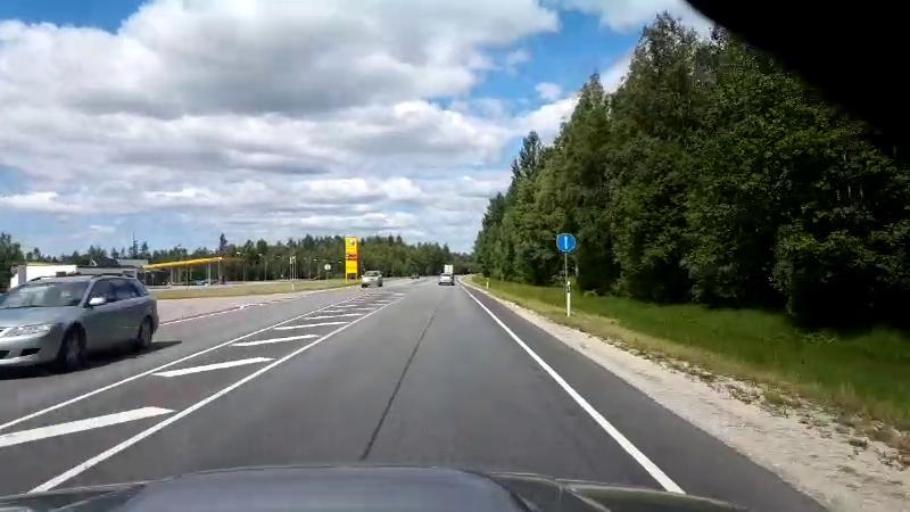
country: EE
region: Paernumaa
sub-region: Halinga vald
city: Parnu-Jaagupi
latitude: 58.7061
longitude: 24.4247
